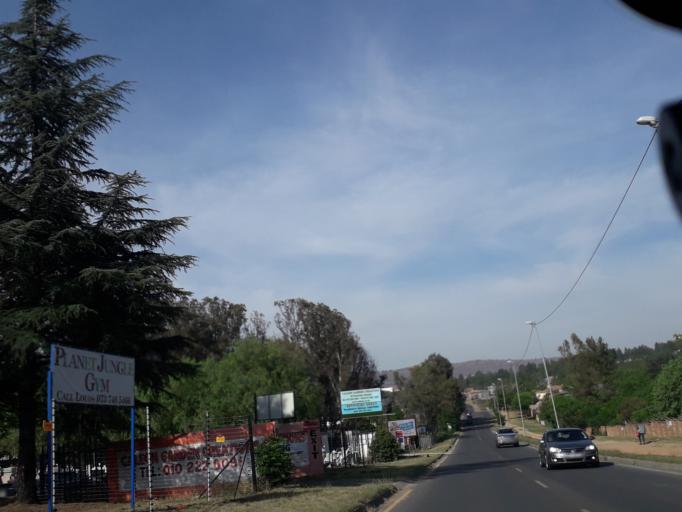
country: ZA
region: Gauteng
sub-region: West Rand District Municipality
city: Muldersdriseloop
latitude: -26.0729
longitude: 27.8873
